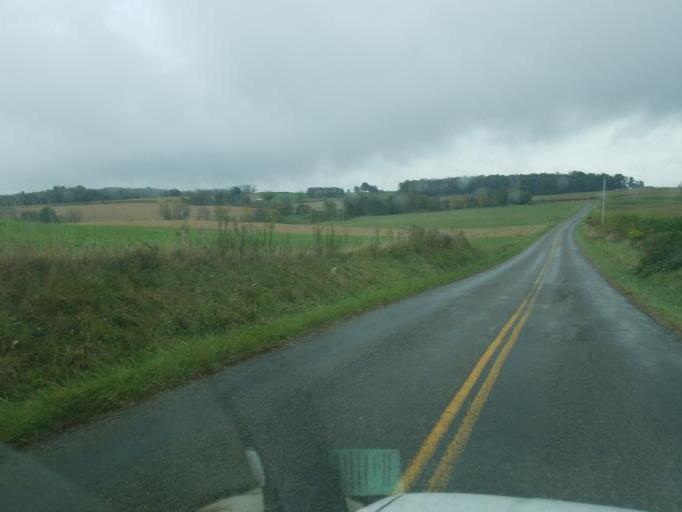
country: US
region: Ohio
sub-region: Holmes County
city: Millersburg
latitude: 40.5506
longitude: -82.0019
